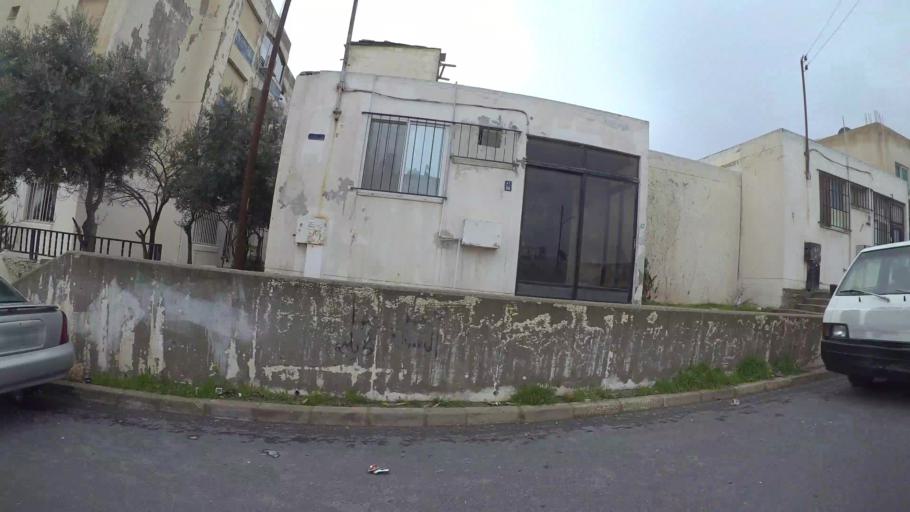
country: JO
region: Amman
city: Al Jubayhah
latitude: 32.0550
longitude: 35.8816
